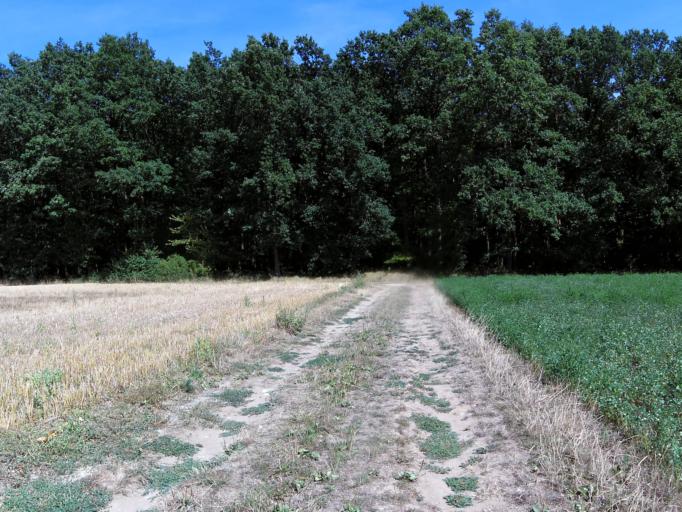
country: DE
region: Bavaria
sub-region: Regierungsbezirk Unterfranken
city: Theilheim
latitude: 49.7466
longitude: 10.0104
